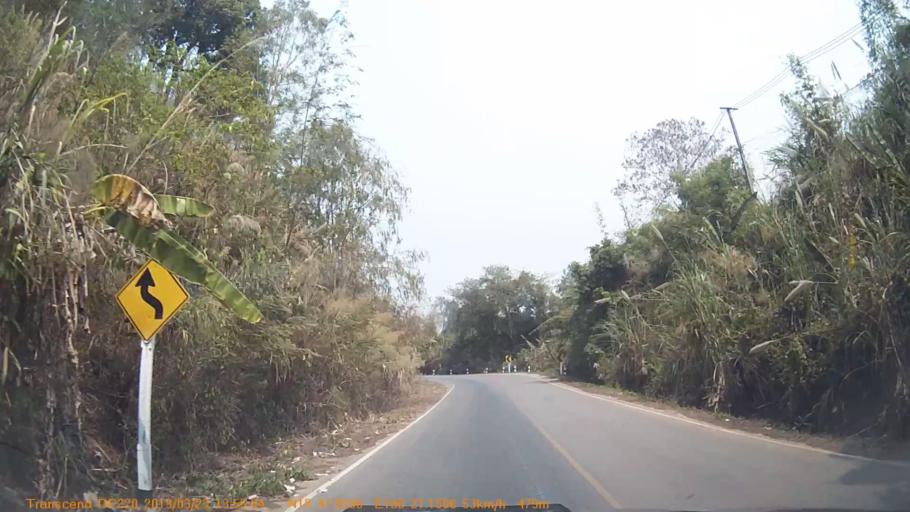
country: TH
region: Chiang Rai
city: Khun Tan
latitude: 19.7990
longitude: 100.3525
